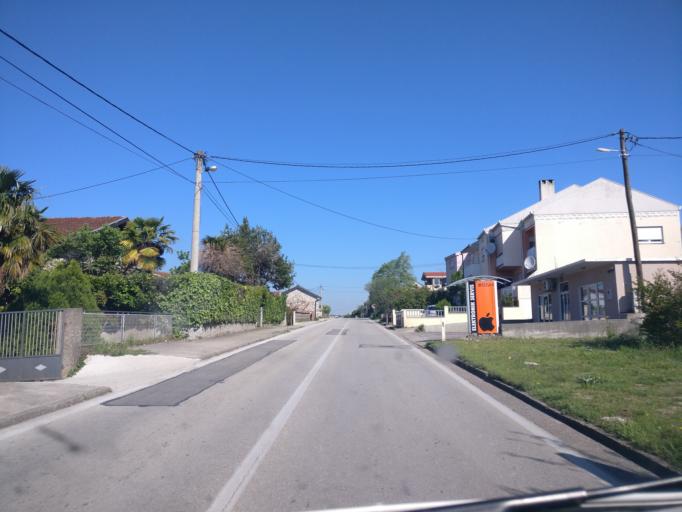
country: BA
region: Federation of Bosnia and Herzegovina
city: Capljina
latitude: 43.1223
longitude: 17.6842
